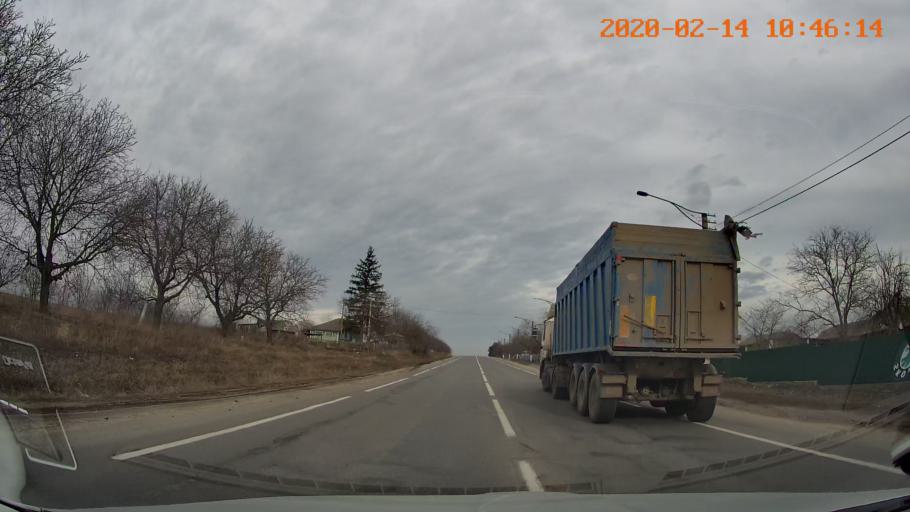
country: MD
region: Riscani
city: Riscani
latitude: 48.0348
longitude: 27.5314
